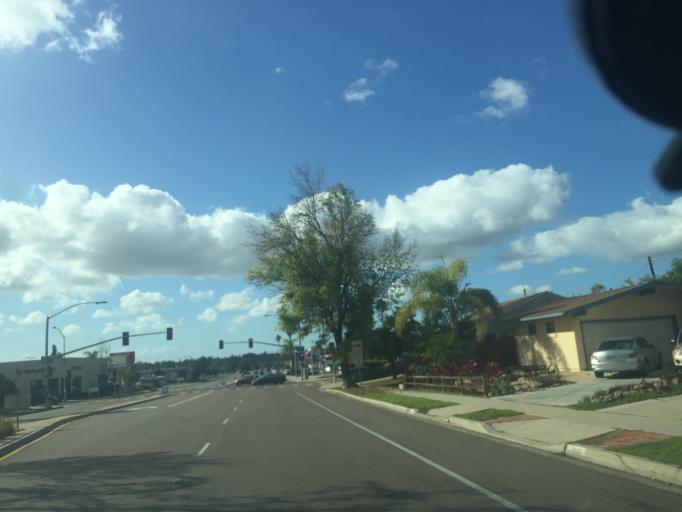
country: US
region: California
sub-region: San Diego County
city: La Mesa
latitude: 32.7934
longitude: -117.0801
